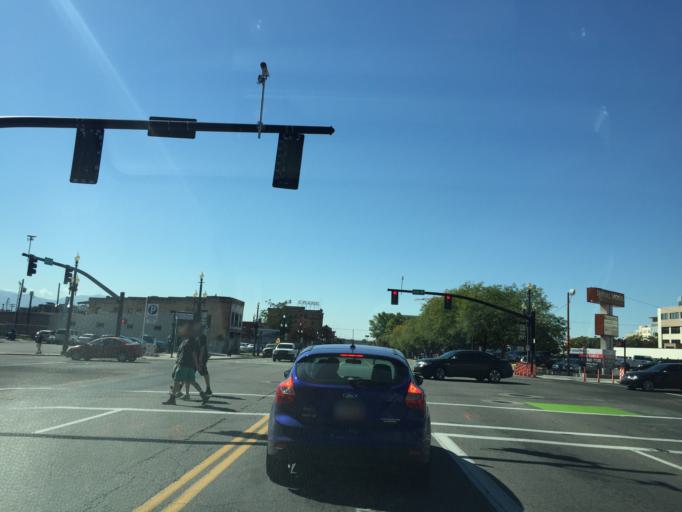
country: US
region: Utah
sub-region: Salt Lake County
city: Salt Lake City
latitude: 40.7650
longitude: -111.8964
